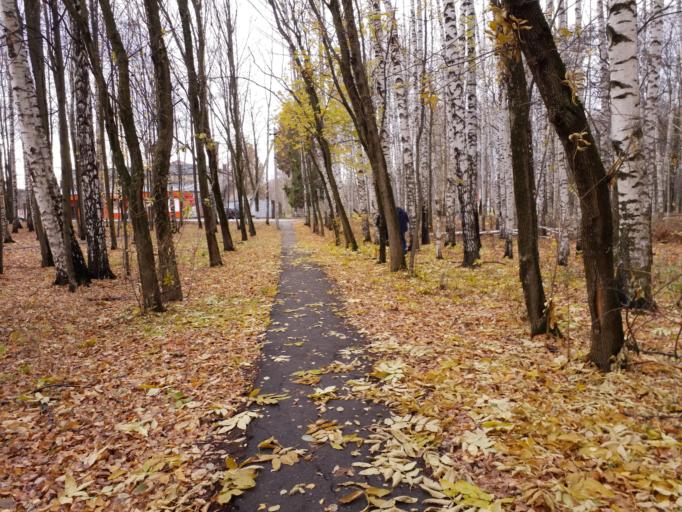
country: RU
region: Moskovskaya
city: Ashukino
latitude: 56.1606
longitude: 37.9458
